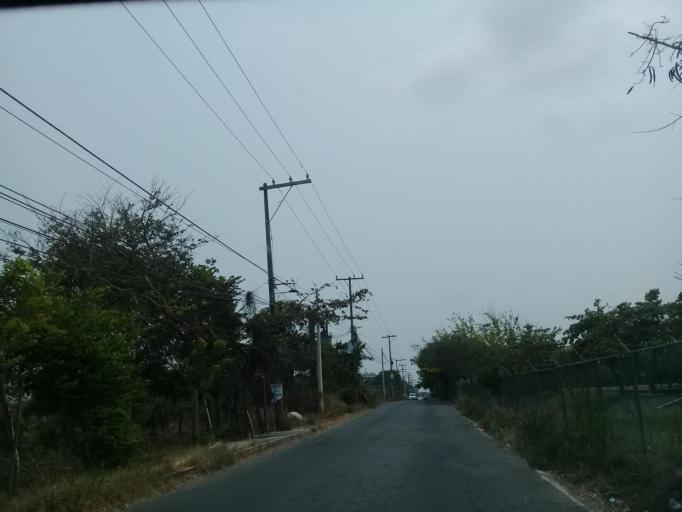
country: MX
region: Veracruz
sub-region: Veracruz
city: Hacienda Sotavento
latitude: 19.1433
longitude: -96.1765
